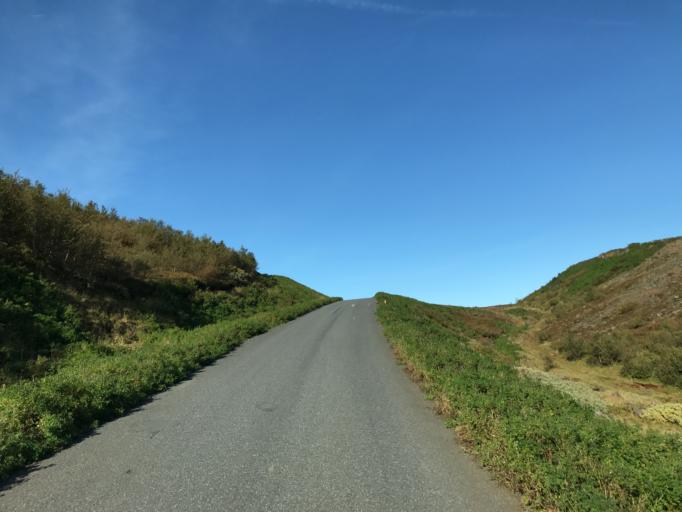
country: IS
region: South
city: Hveragerdi
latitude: 64.1310
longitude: -21.2510
